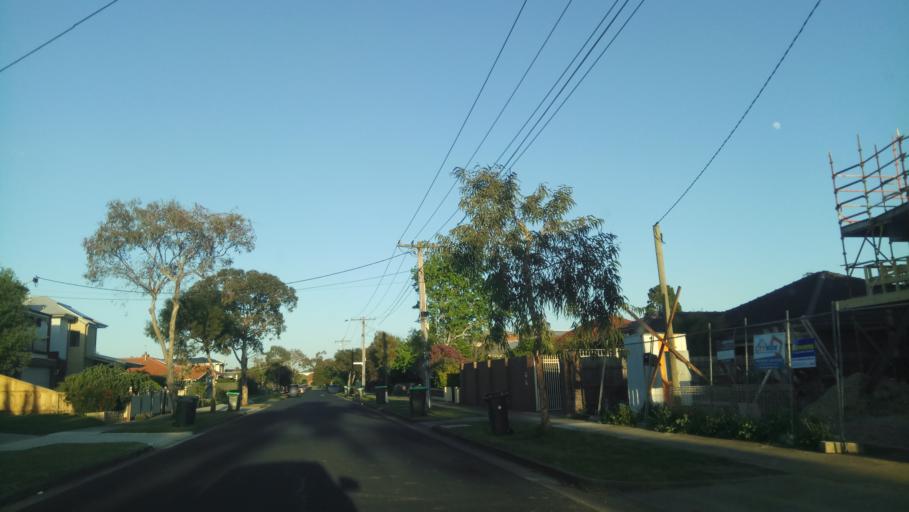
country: AU
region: Victoria
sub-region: Hobsons Bay
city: Altona
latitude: -37.8680
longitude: 144.8172
